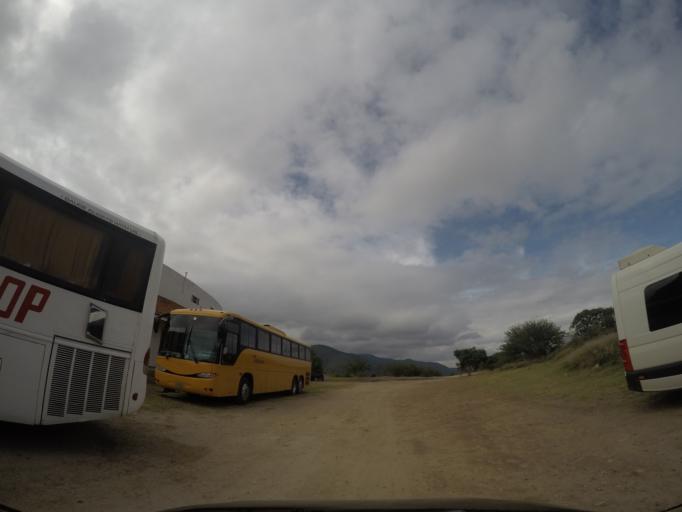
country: MX
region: Oaxaca
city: San Lorenzo Albarradas
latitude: 16.8677
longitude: -96.2764
